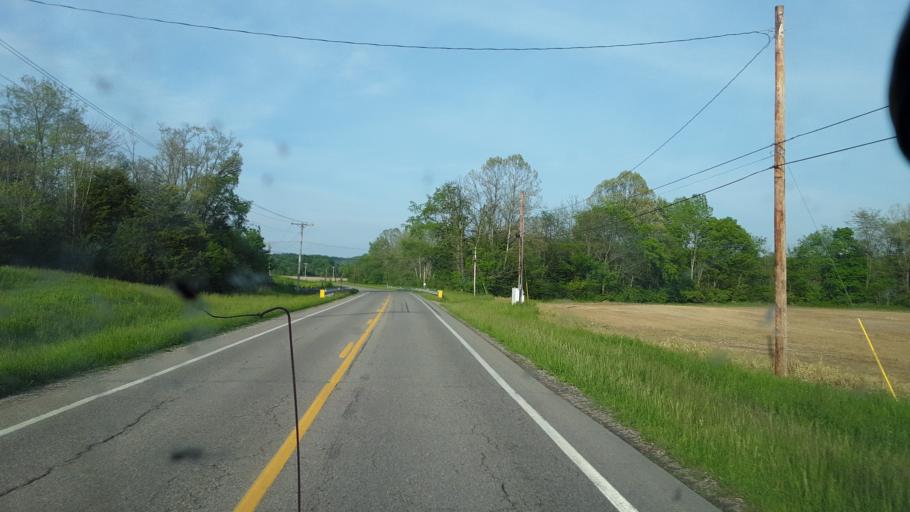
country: US
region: Ohio
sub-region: Ross County
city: Kingston
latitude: 39.4949
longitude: -82.7176
